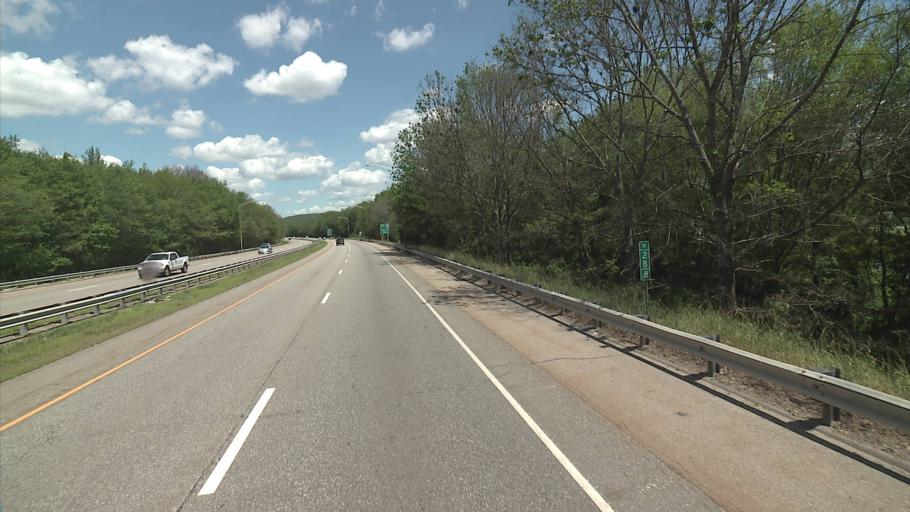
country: US
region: Connecticut
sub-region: Windham County
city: Plainfield
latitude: 41.6699
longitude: -71.9103
